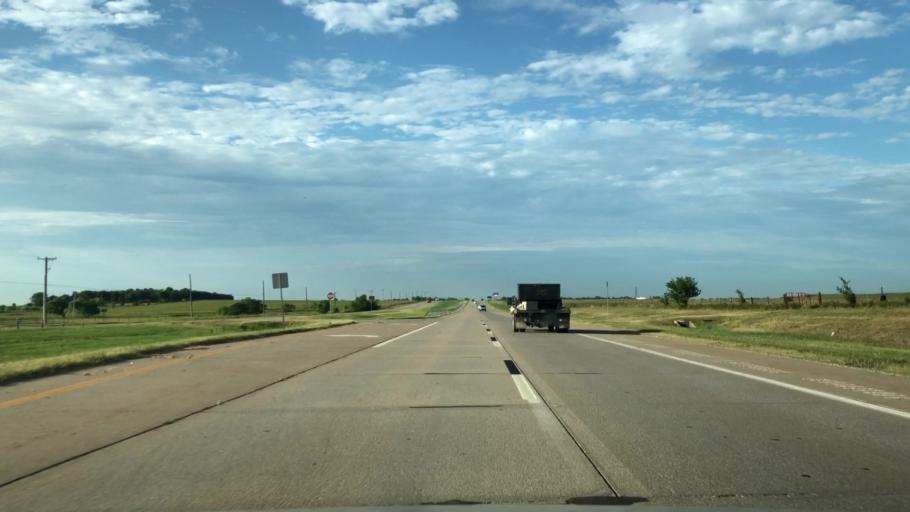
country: US
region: Oklahoma
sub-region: Osage County
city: Skiatook
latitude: 36.3880
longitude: -95.9205
